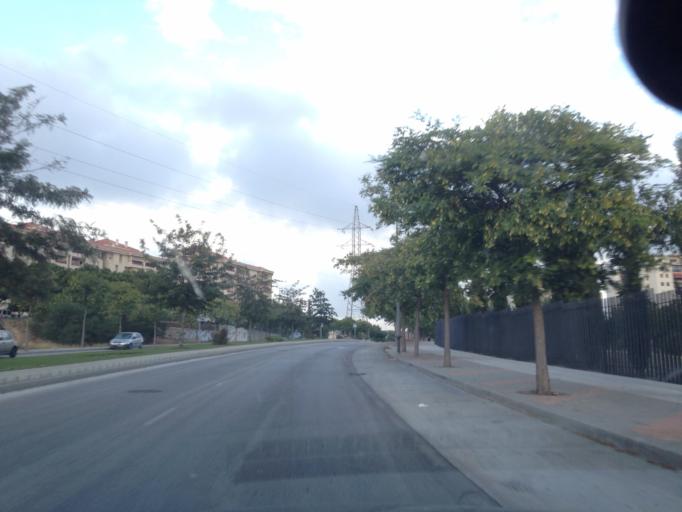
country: ES
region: Andalusia
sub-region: Provincia de Malaga
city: Malaga
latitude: 36.7294
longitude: -4.4706
